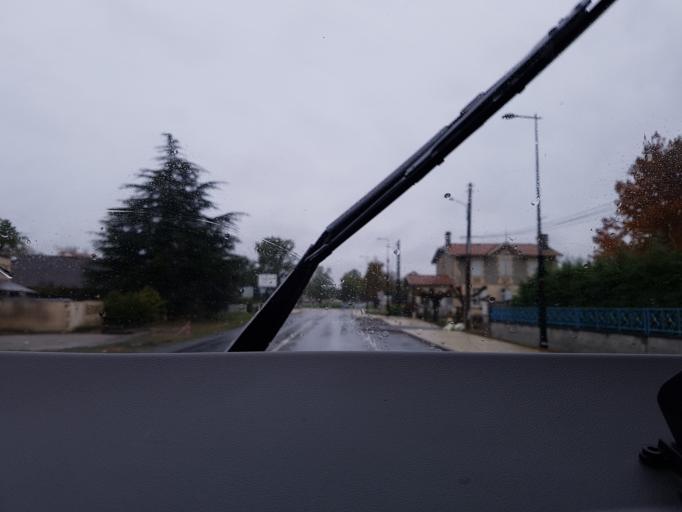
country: FR
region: Aquitaine
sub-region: Departement de la Gironde
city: Belin-Beliet
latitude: 44.5162
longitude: -0.7937
